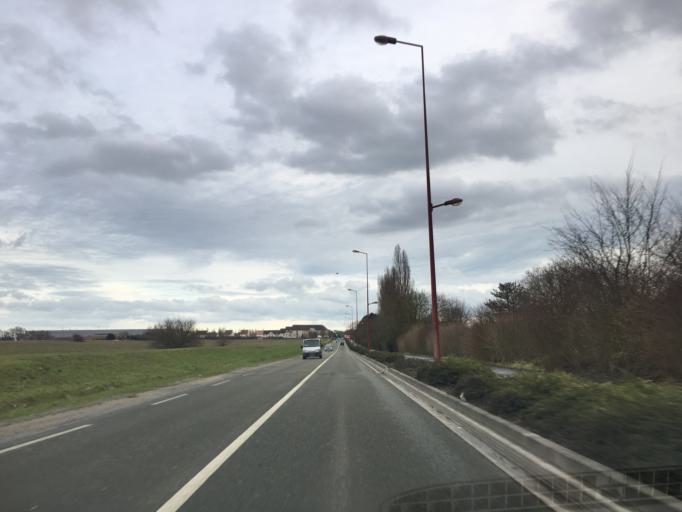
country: FR
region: Ile-de-France
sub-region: Departement du Val-d'Oise
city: Gonesse
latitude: 48.9967
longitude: 2.4373
